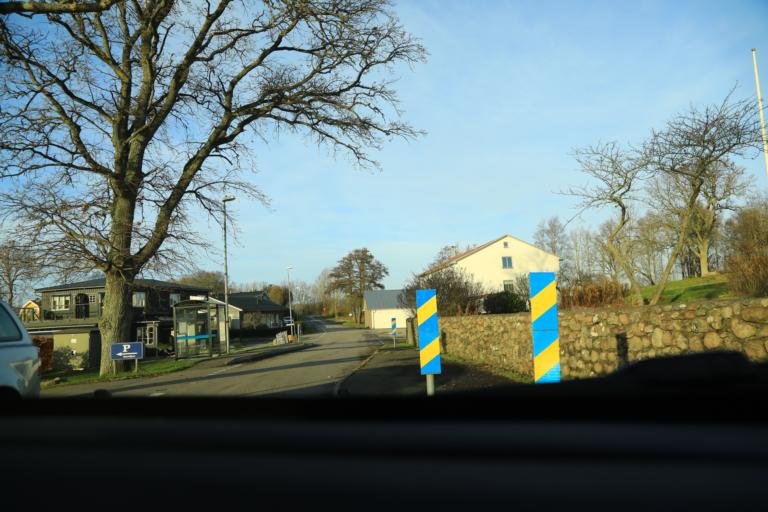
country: SE
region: Halland
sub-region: Varbergs Kommun
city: Varberg
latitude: 57.1907
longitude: 12.2205
